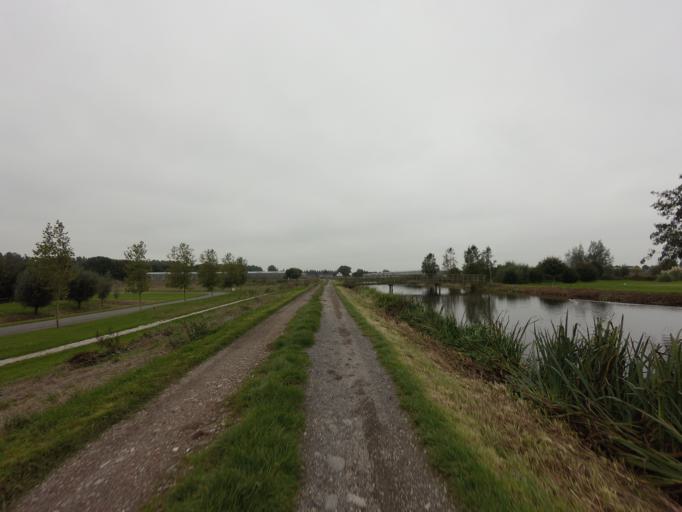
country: NL
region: South Holland
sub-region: Gemeente Nieuwkoop
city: Nieuwkoop
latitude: 52.1874
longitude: 4.7396
